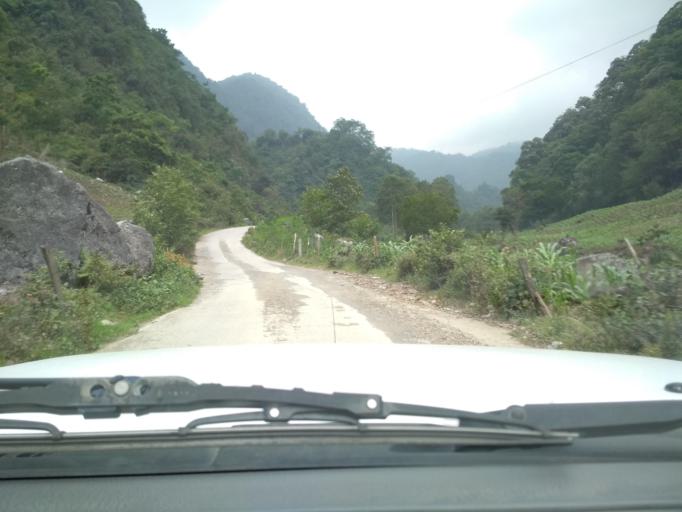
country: MX
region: Veracruz
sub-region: La Perla
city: Metlac Hernandez (Metlac Primero)
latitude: 18.9832
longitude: -97.1328
